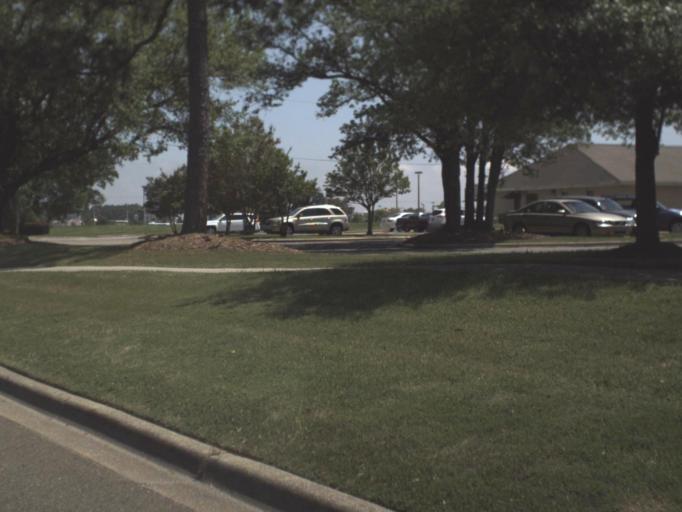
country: US
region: Florida
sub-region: Escambia County
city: Ferry Pass
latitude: 30.4818
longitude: -87.2102
